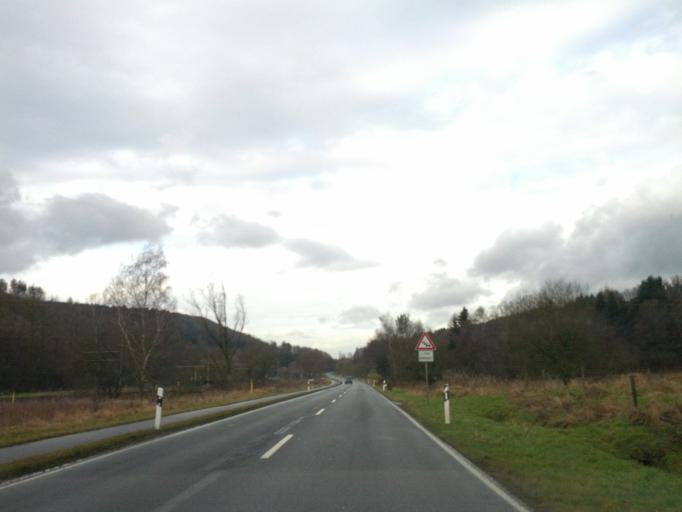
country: DE
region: Hesse
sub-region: Regierungsbezirk Kassel
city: Helsa
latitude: 51.2657
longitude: 9.6765
